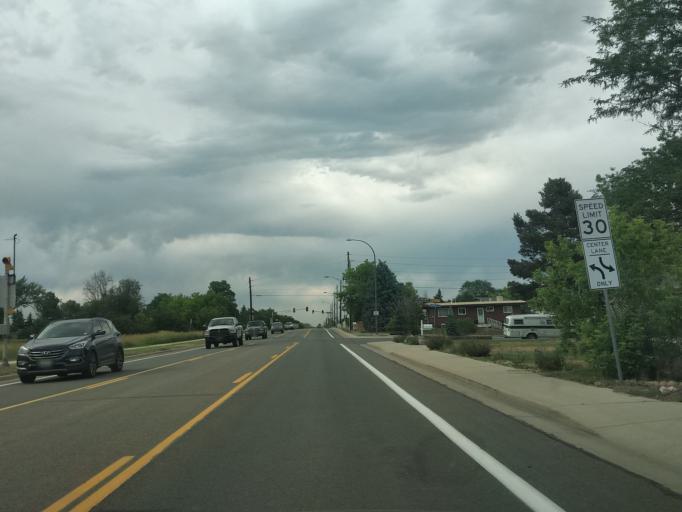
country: US
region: Colorado
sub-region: Jefferson County
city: Lakewood
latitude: 39.7027
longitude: -105.1002
